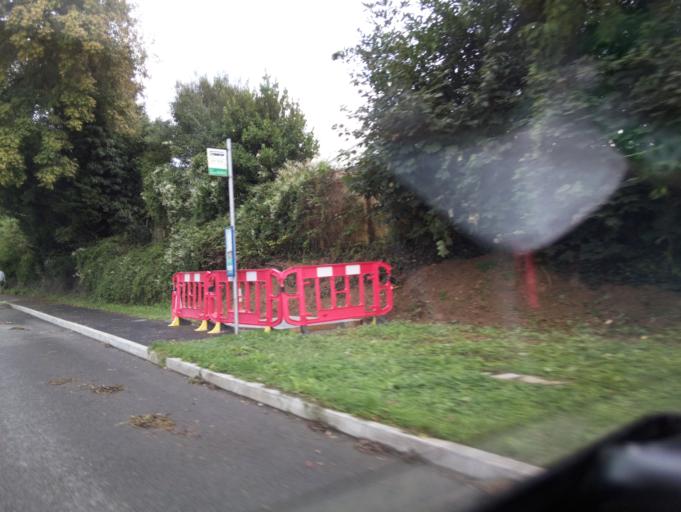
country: GB
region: England
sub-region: Devon
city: Modbury
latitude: 50.3502
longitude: -3.8911
